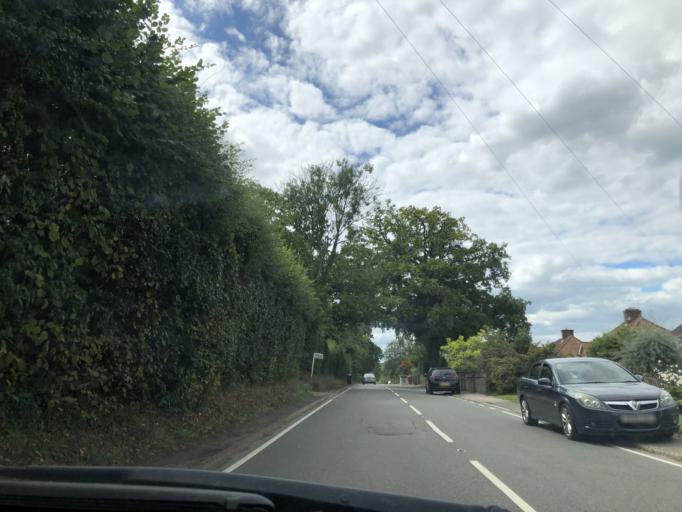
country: GB
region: England
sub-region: East Sussex
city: Forest Row
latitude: 51.0941
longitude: 0.0941
